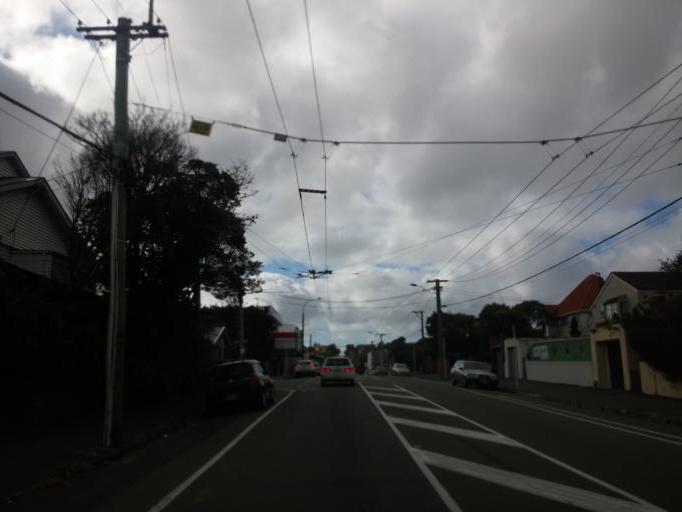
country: NZ
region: Wellington
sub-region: Wellington City
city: Kelburn
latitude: -41.2853
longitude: 174.7352
